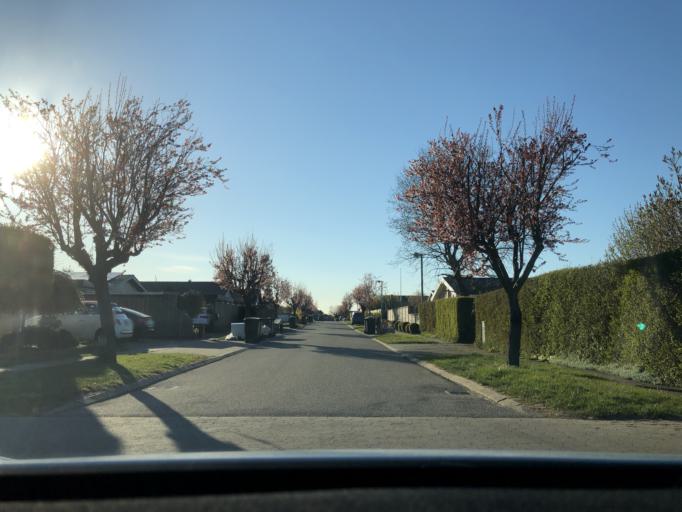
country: DK
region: Zealand
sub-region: Greve Kommune
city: Greve
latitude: 55.5813
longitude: 12.2824
